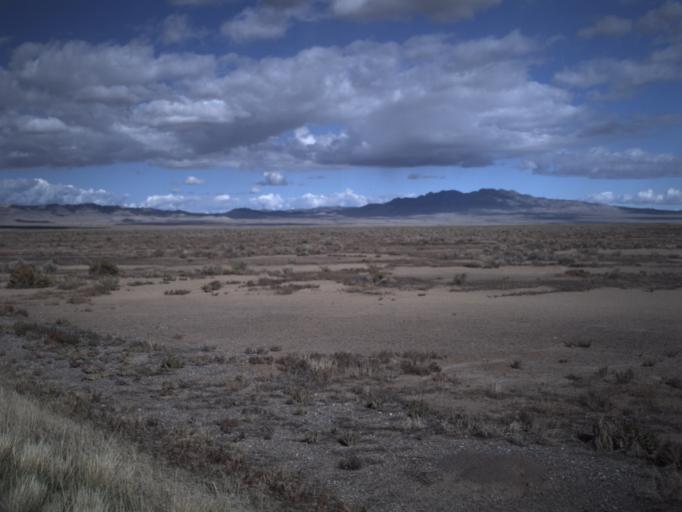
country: US
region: Utah
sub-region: Beaver County
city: Milford
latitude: 38.5281
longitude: -113.6703
